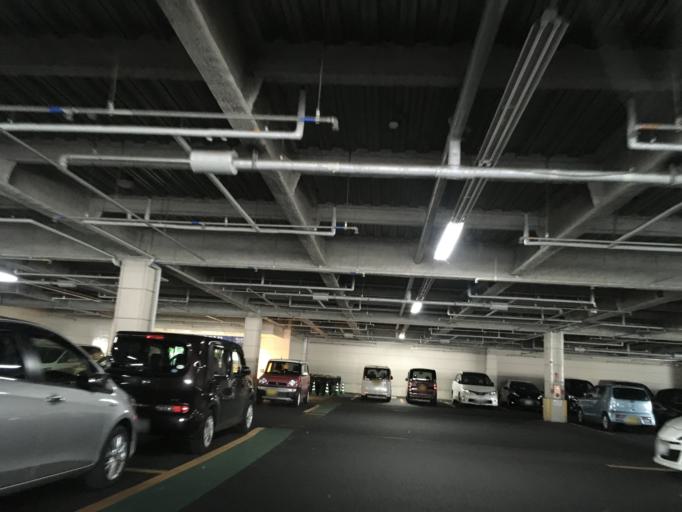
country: JP
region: Miyagi
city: Wakuya
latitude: 38.6841
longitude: 141.1851
